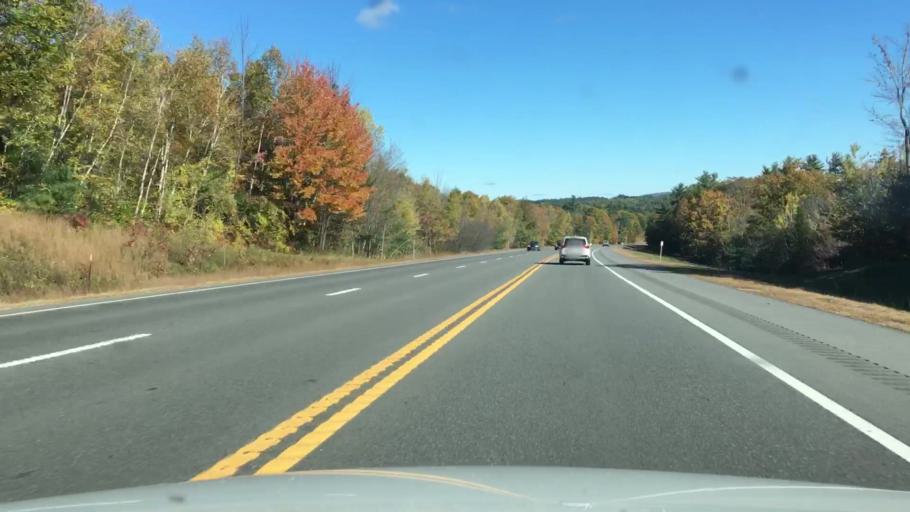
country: US
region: New Hampshire
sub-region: Strafford County
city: Farmington
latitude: 43.4416
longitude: -71.0047
